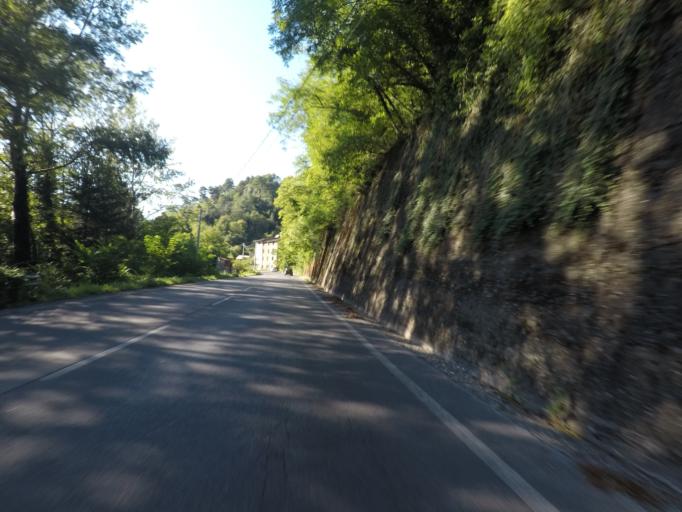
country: IT
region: Tuscany
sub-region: Provincia di Lucca
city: Massarosa
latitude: 43.9028
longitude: 10.3752
